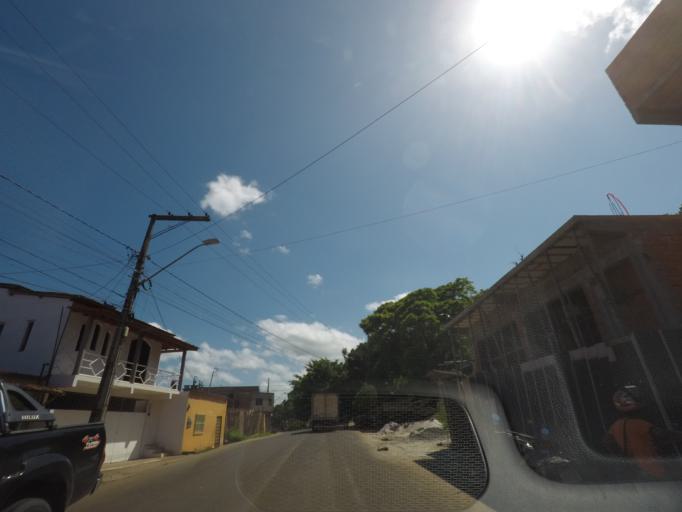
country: BR
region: Bahia
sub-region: Itubera
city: Itubera
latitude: -13.7423
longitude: -39.1508
